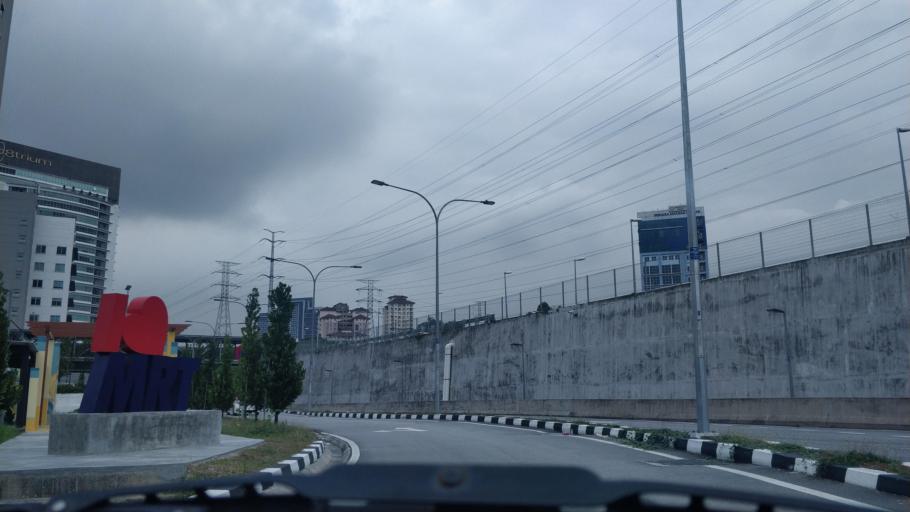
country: MY
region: Selangor
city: Kuang
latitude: 3.1976
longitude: 101.6069
